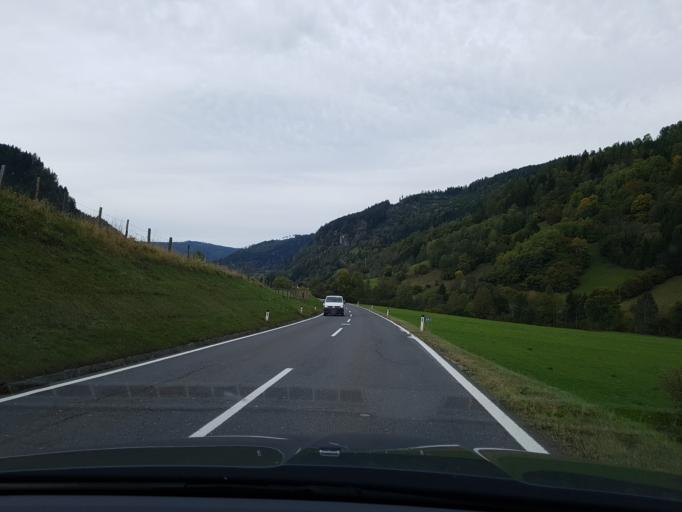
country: AT
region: Salzburg
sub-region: Politischer Bezirk Tamsweg
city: Ramingstein
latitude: 47.0697
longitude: 13.8753
